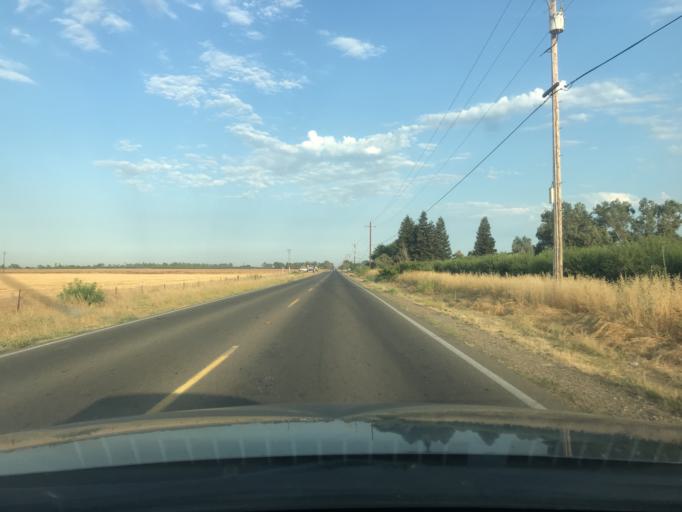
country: US
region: California
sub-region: Merced County
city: Merced
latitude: 37.3611
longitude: -120.4873
